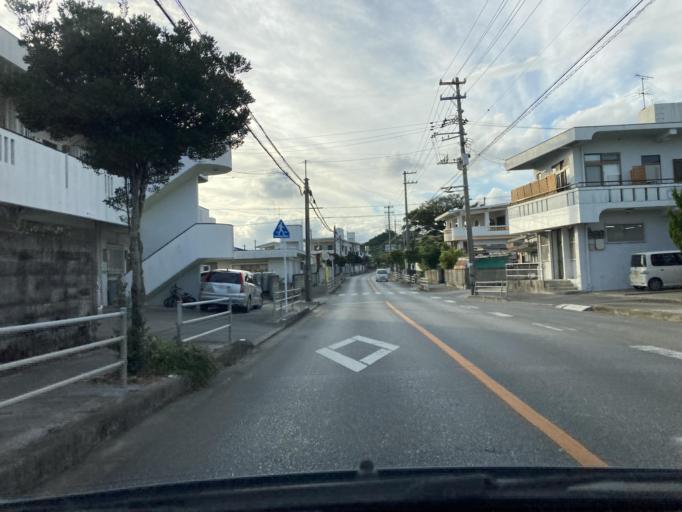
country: JP
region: Okinawa
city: Tomigusuku
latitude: 26.1507
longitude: 127.7078
